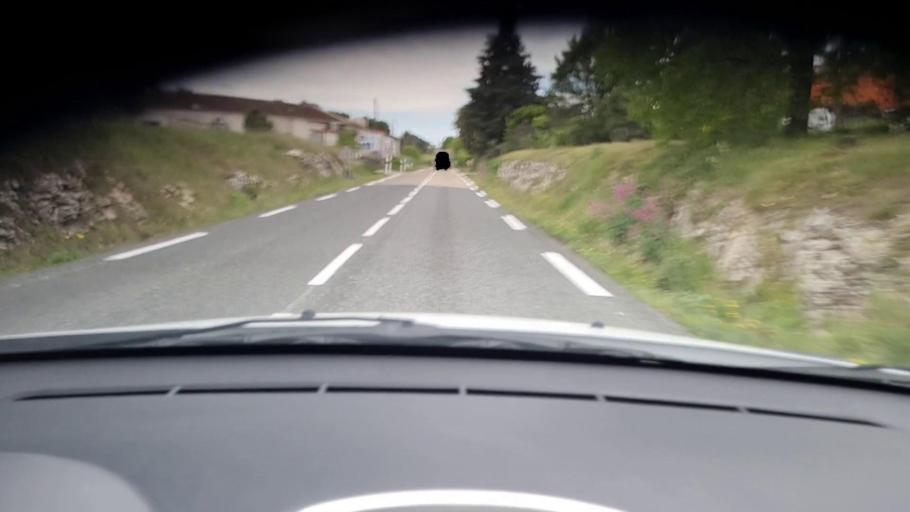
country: FR
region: Languedoc-Roussillon
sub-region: Departement du Gard
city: Poulx
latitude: 43.8841
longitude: 4.3795
